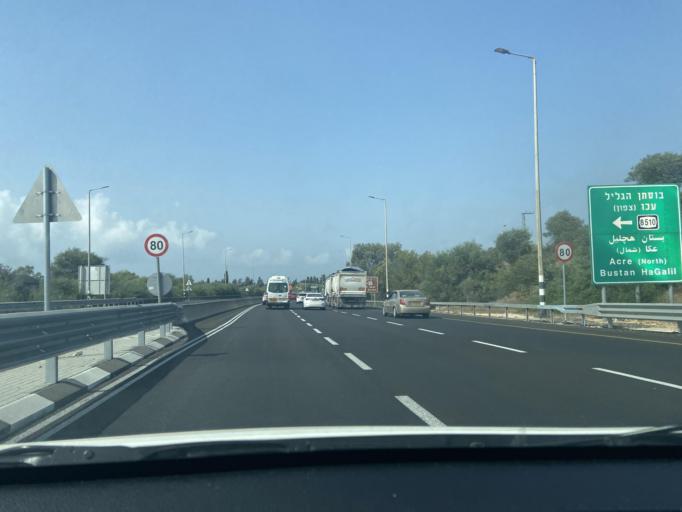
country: IL
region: Northern District
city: `Akko
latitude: 32.9492
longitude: 35.0923
